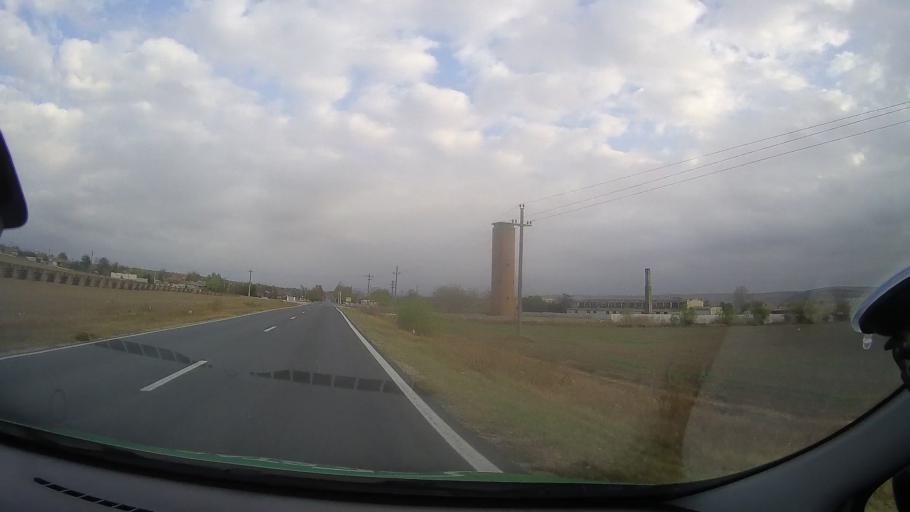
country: RO
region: Constanta
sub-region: Comuna Mircea Voda
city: Satu Nou
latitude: 44.2698
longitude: 28.2147
